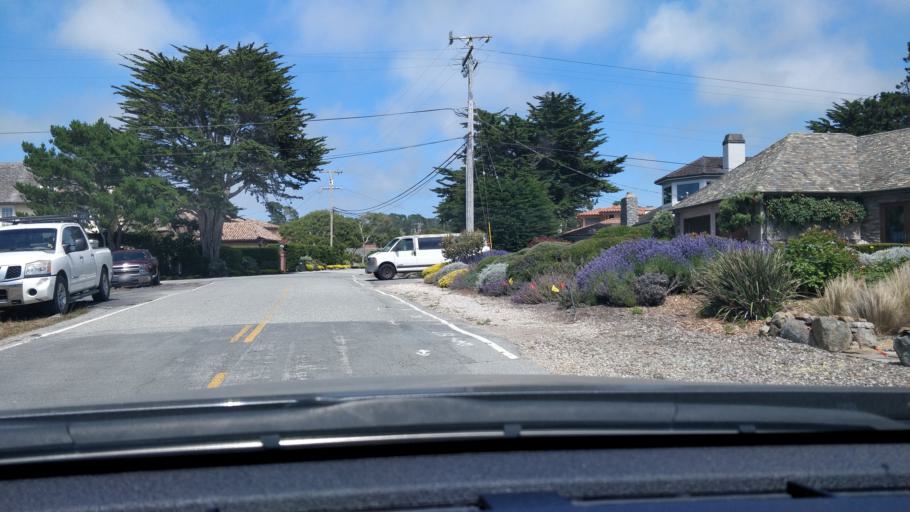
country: US
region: California
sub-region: Monterey County
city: Del Monte Forest
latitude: 36.5903
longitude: -121.9588
